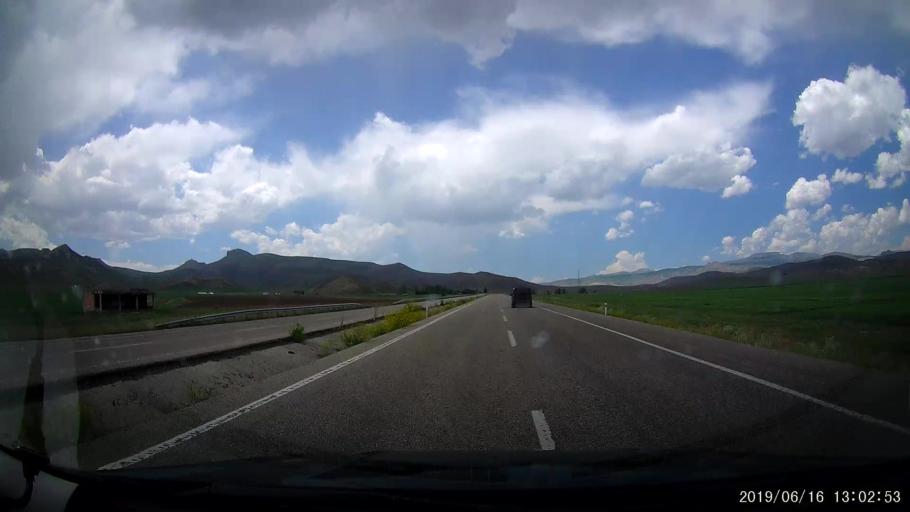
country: TR
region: Agri
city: Sulucem
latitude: 39.5773
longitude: 43.8040
